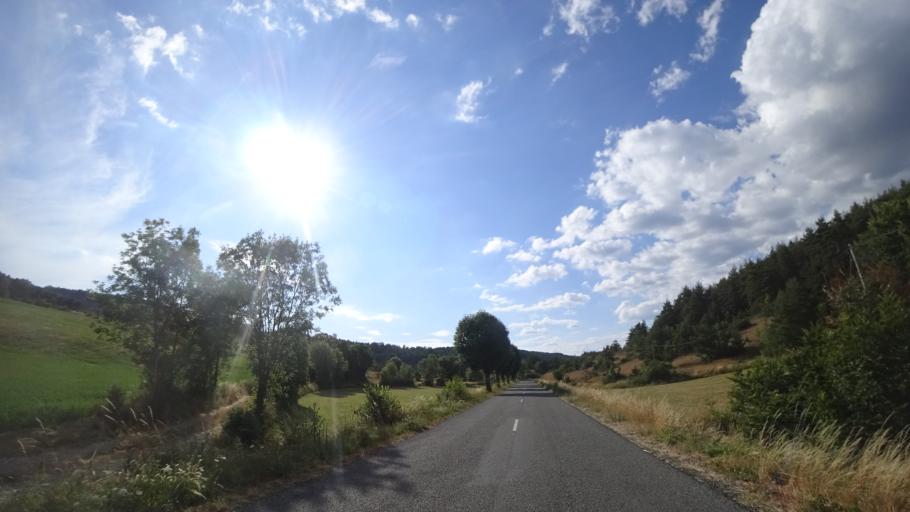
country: FR
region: Languedoc-Roussillon
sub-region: Departement de la Lozere
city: Chanac
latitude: 44.3915
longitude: 3.2997
